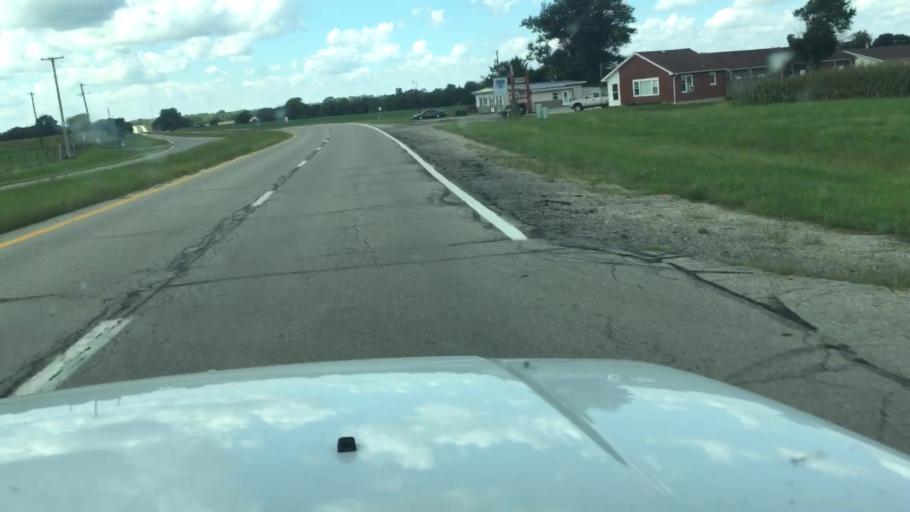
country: US
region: Ohio
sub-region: Madison County
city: Choctaw Lake
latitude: 39.9332
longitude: -83.4996
